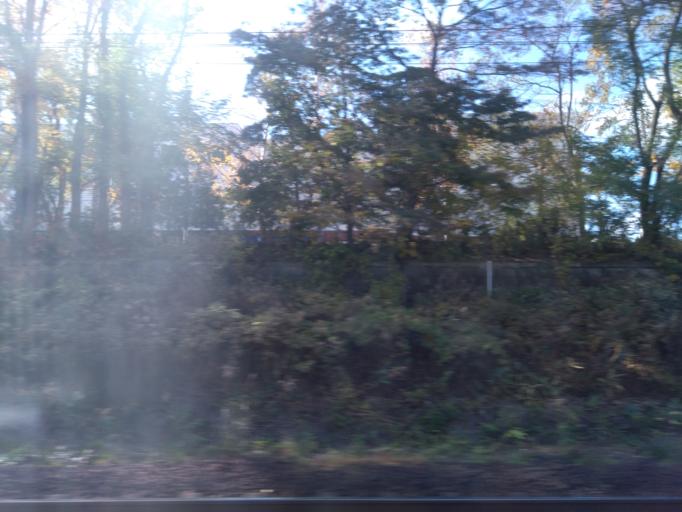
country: JP
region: Hokkaido
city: Kitahiroshima
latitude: 42.9749
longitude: 141.5637
